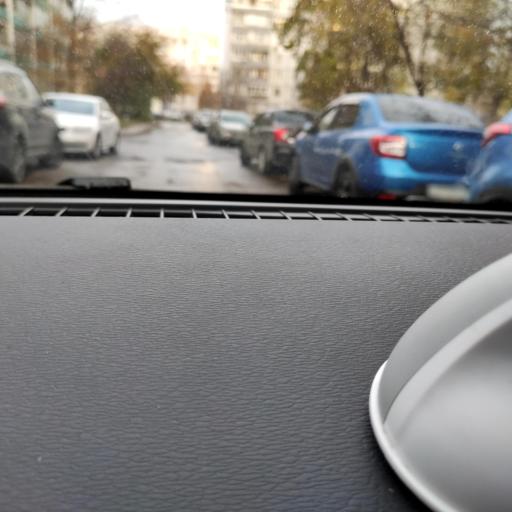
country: RU
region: Samara
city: Petra-Dubrava
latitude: 53.2246
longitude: 50.2709
